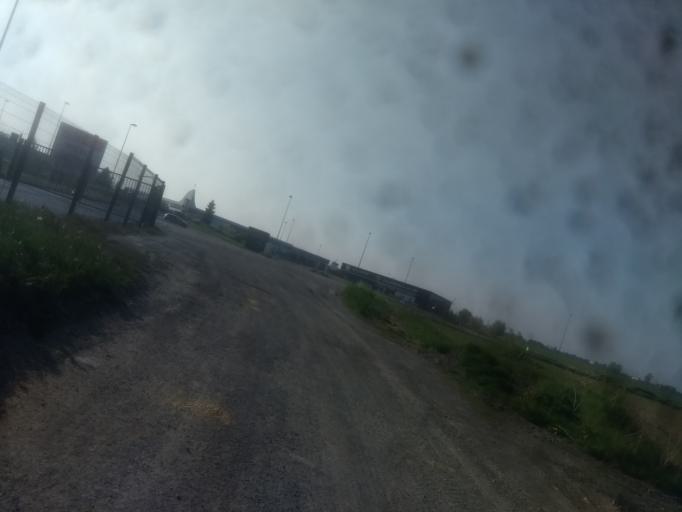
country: FR
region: Nord-Pas-de-Calais
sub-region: Departement du Pas-de-Calais
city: Beaurains
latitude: 50.2684
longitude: 2.8022
